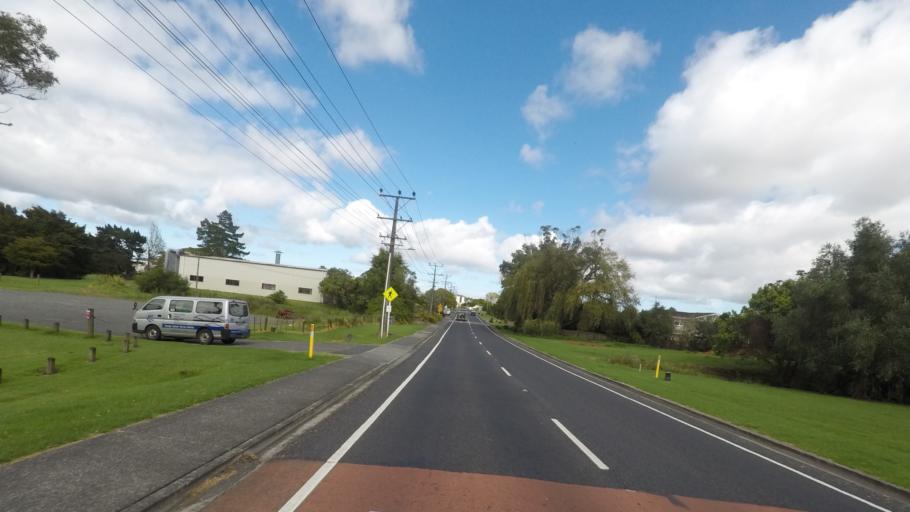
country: NZ
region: Auckland
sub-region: Auckland
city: Muriwai Beach
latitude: -36.7705
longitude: 174.5489
